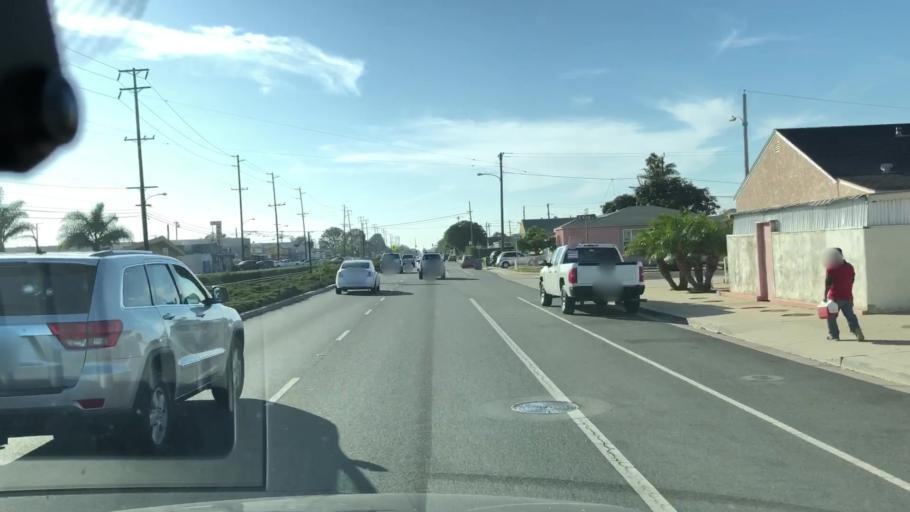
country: US
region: California
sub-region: Ventura County
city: Oxnard
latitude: 34.1902
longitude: -119.1852
